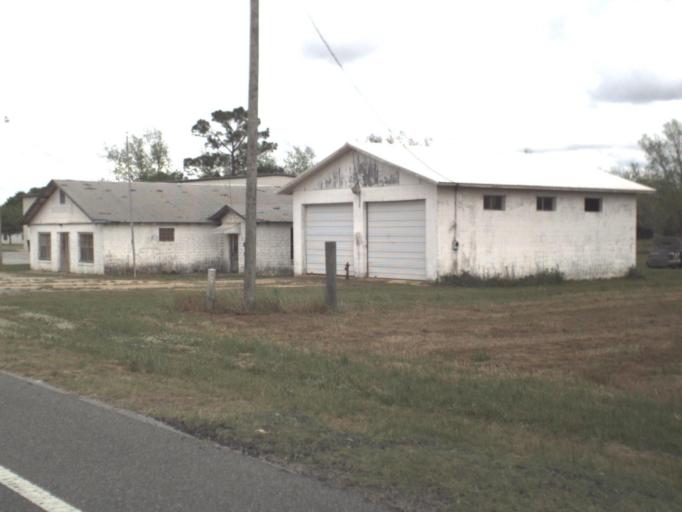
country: US
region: Florida
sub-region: Santa Rosa County
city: Point Baker
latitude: 30.7822
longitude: -87.0925
